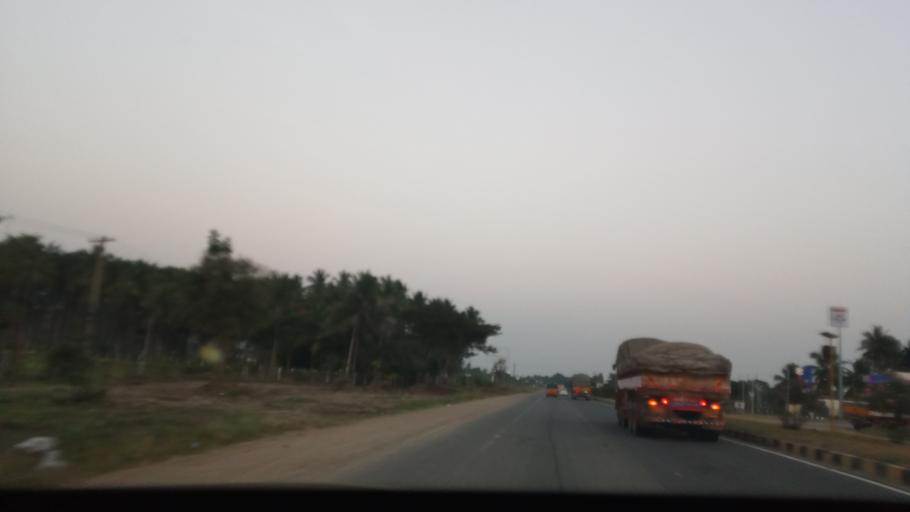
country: IN
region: Tamil Nadu
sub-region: Salem
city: Belur
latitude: 11.6527
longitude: 78.3670
